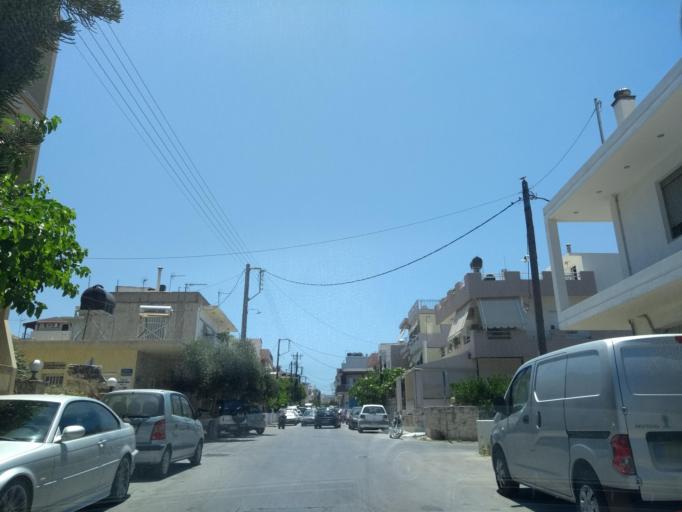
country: GR
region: Crete
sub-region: Nomos Irakleiou
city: Nea Alikarnassos
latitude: 35.3363
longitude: 25.1606
